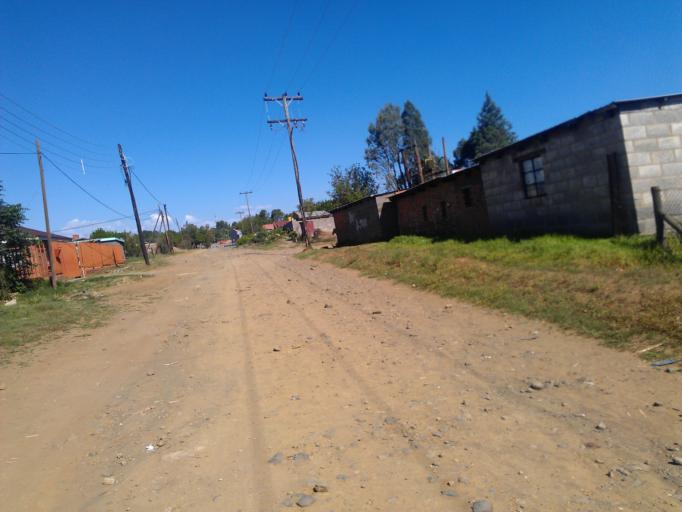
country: LS
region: Maseru
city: Maseru
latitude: -29.3017
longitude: 27.4649
